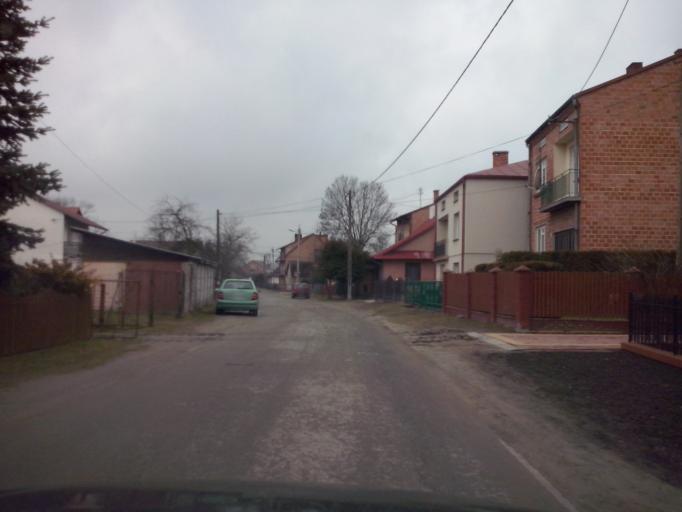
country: PL
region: Subcarpathian Voivodeship
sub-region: Powiat nizanski
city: Krzeszow
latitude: 50.4043
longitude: 22.3406
